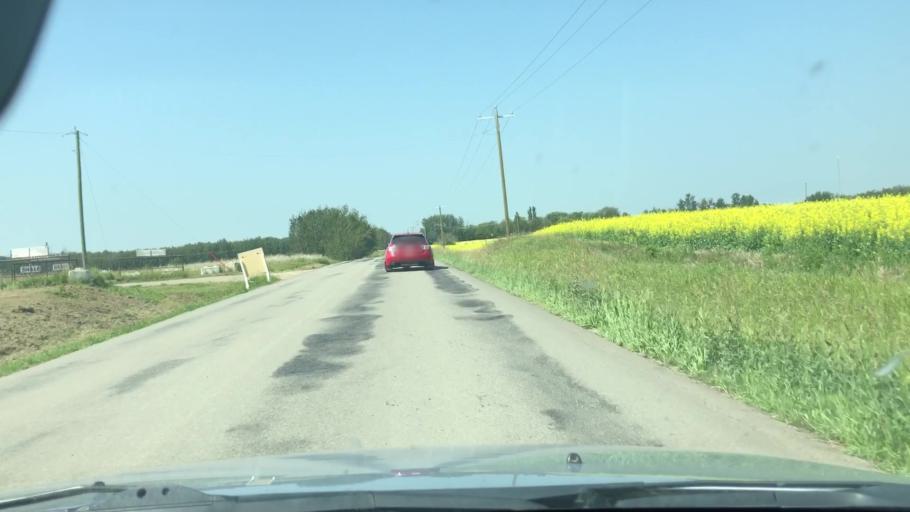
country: CA
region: Alberta
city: Devon
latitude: 53.5122
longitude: -113.7183
